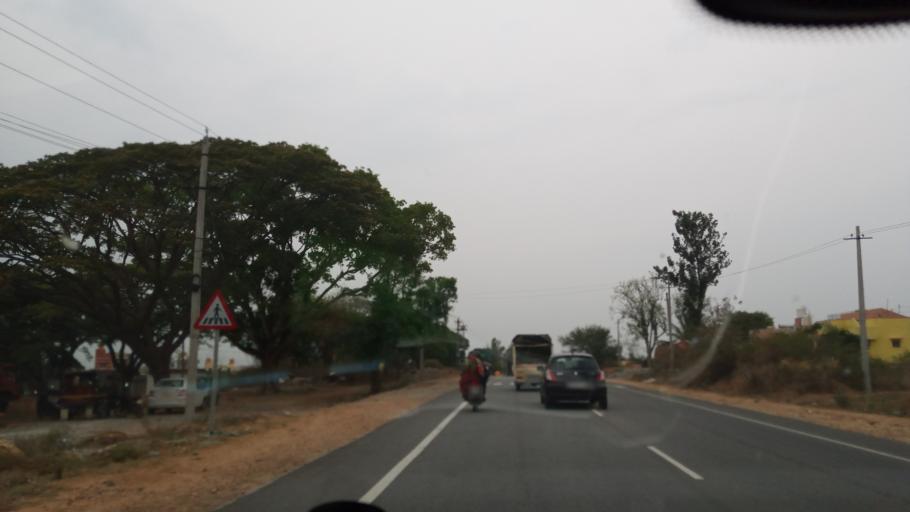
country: IN
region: Karnataka
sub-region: Mandya
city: Belluru
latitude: 12.9363
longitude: 76.7503
